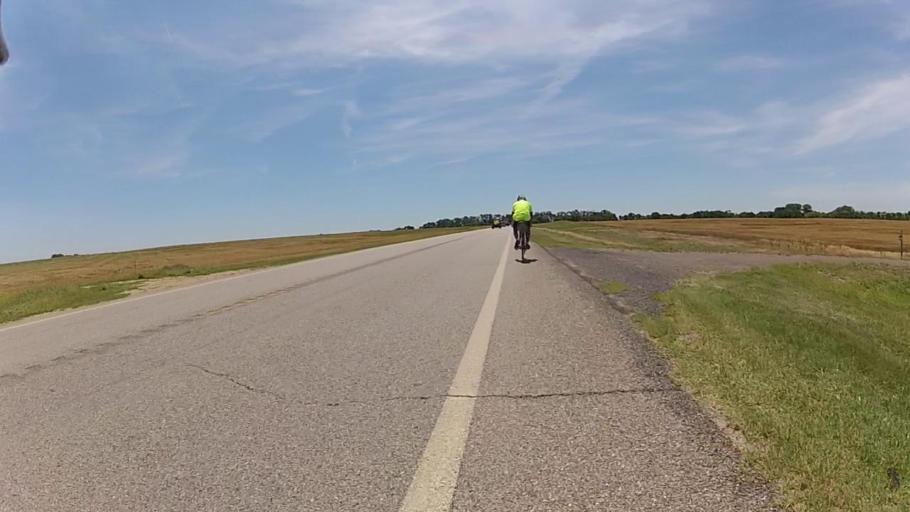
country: US
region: Kansas
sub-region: Barber County
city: Medicine Lodge
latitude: 37.2588
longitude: -98.5263
